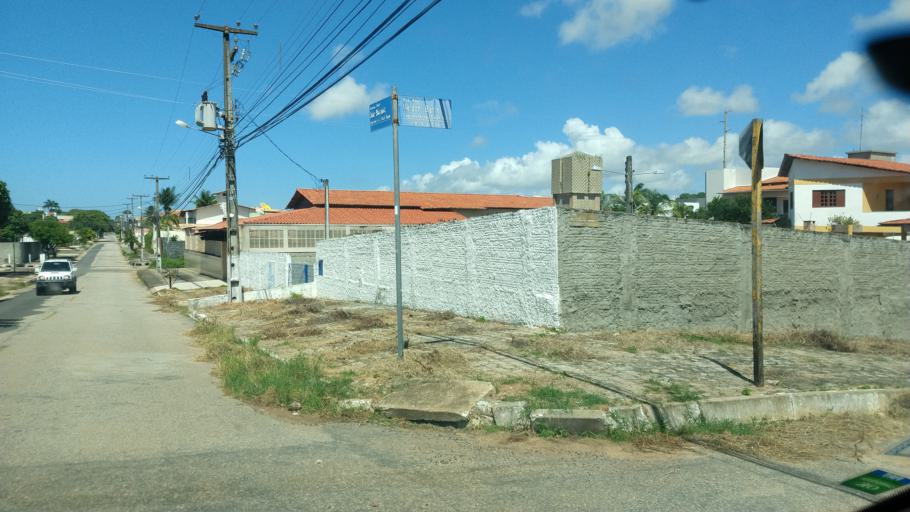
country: BR
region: Rio Grande do Norte
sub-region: Natal
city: Natal
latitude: -5.8448
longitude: -35.2026
